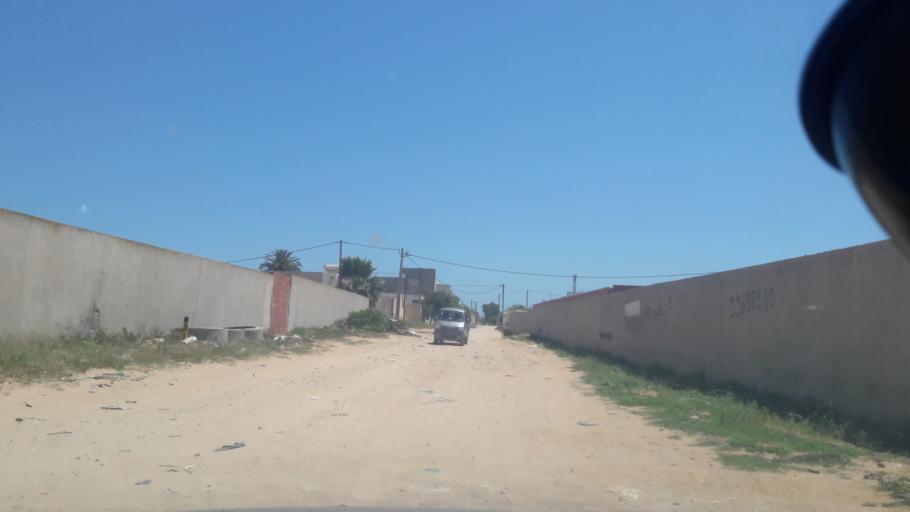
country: TN
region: Safaqis
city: Al Qarmadah
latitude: 34.8014
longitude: 10.7503
